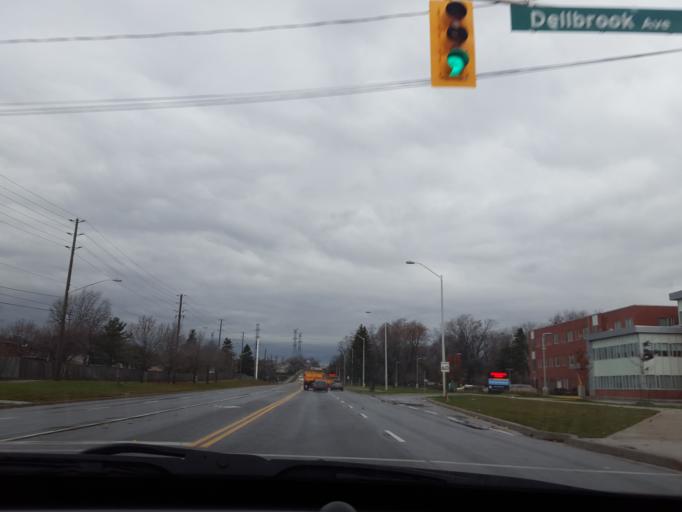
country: CA
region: Ontario
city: Ajax
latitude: 43.8588
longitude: -79.0792
